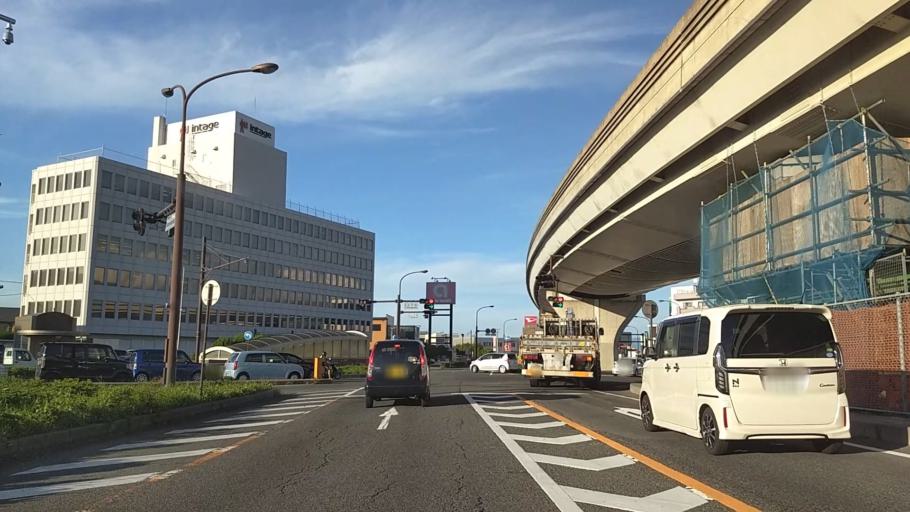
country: JP
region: Nagano
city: Nagano-shi
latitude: 36.6284
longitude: 138.2013
